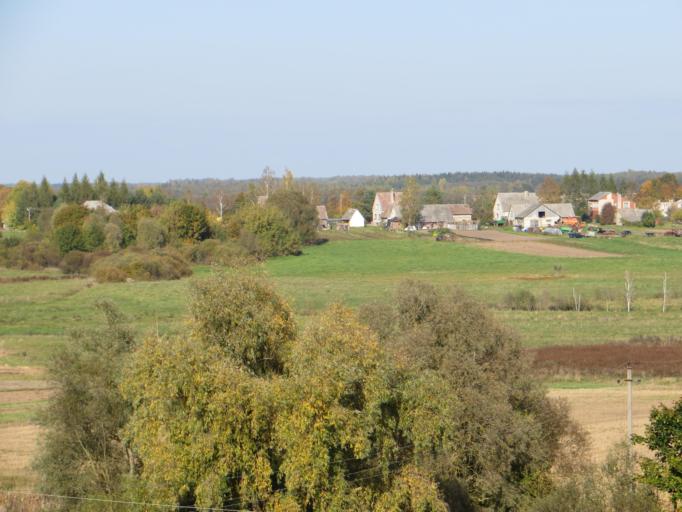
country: LT
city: Obeliai
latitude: 56.0141
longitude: 25.2312
